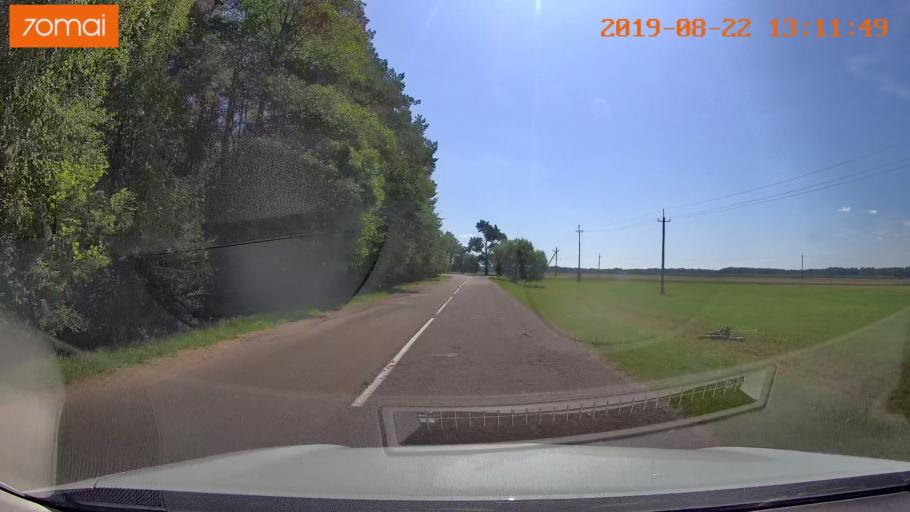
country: BY
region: Minsk
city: Prawdzinski
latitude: 53.2748
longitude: 27.8547
